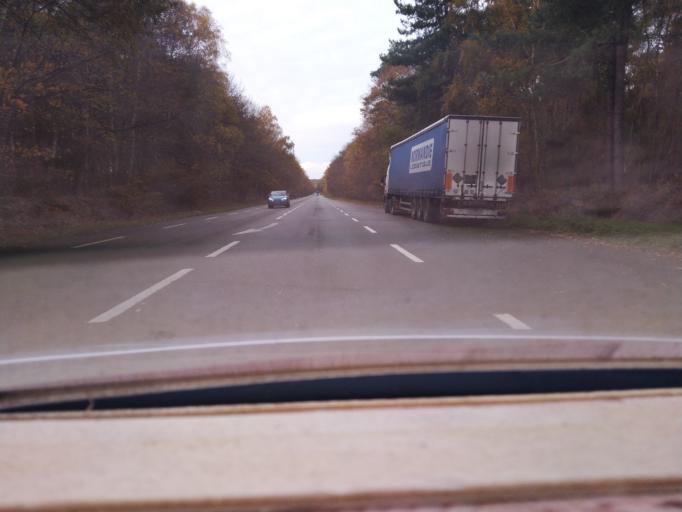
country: FR
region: Haute-Normandie
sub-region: Departement de la Seine-Maritime
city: Montigny
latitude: 49.4451
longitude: 1.0058
